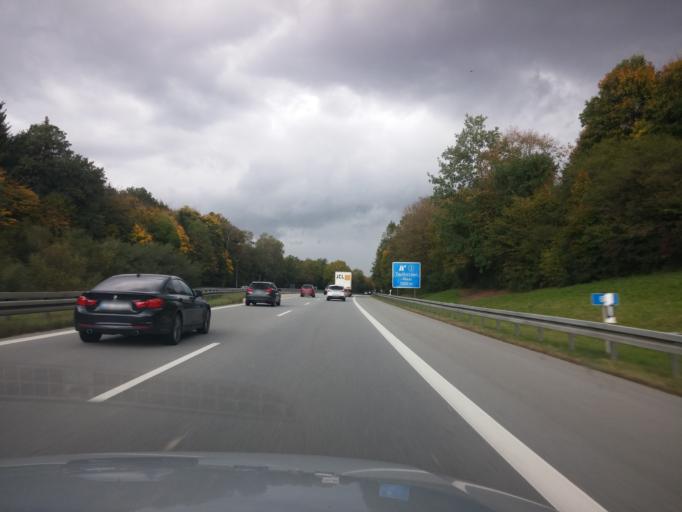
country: DE
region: Bavaria
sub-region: Upper Bavaria
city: Oberhaching
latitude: 48.0421
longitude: 11.5989
